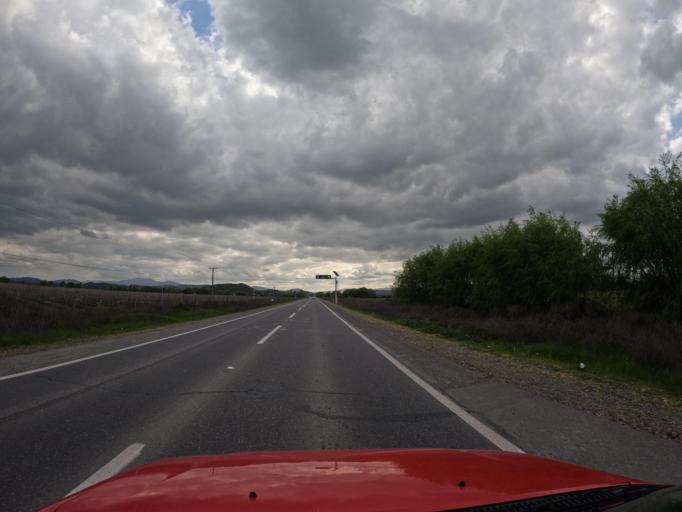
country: CL
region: Maule
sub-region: Provincia de Linares
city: San Javier
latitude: -35.6322
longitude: -71.7139
